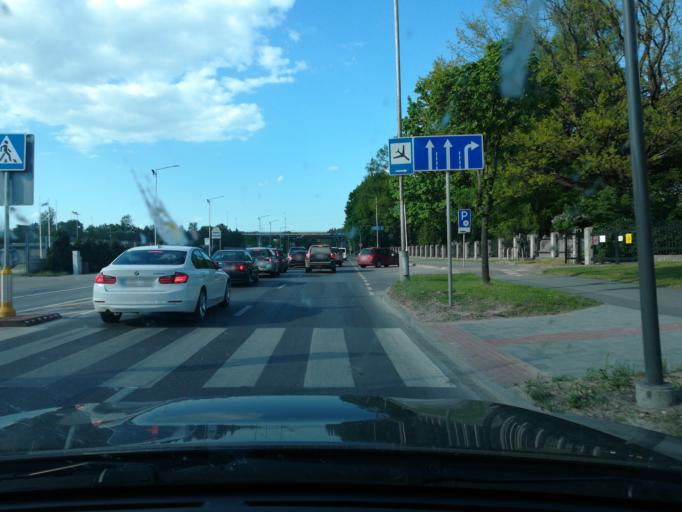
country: LT
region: Kauno apskritis
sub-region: Kaunas
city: Eiguliai
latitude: 54.9339
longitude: 23.9181
